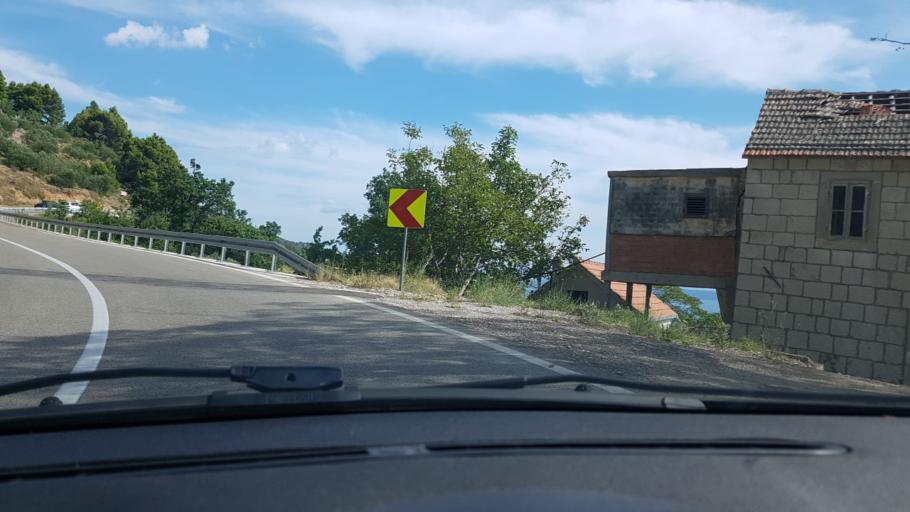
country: HR
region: Splitsko-Dalmatinska
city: Tucepi
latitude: 43.2767
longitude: 17.0631
